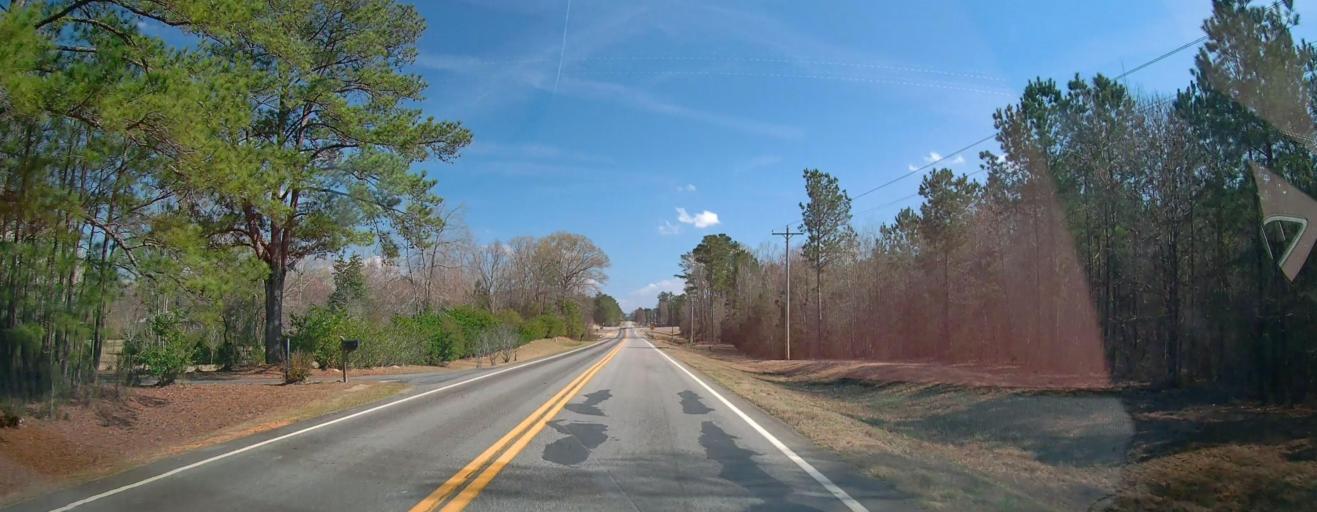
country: US
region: Georgia
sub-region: Wilkinson County
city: Gordon
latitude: 32.8964
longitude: -83.3635
